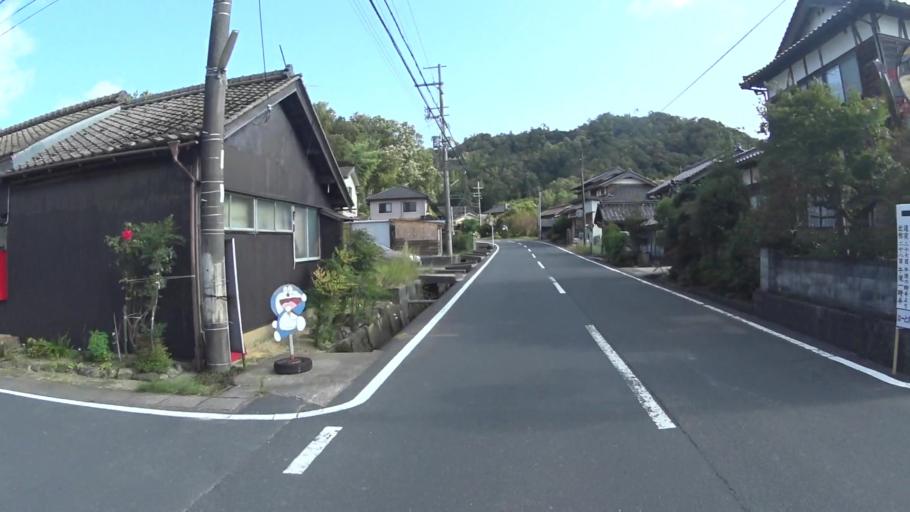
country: JP
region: Kyoto
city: Miyazu
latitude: 35.5766
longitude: 135.1019
